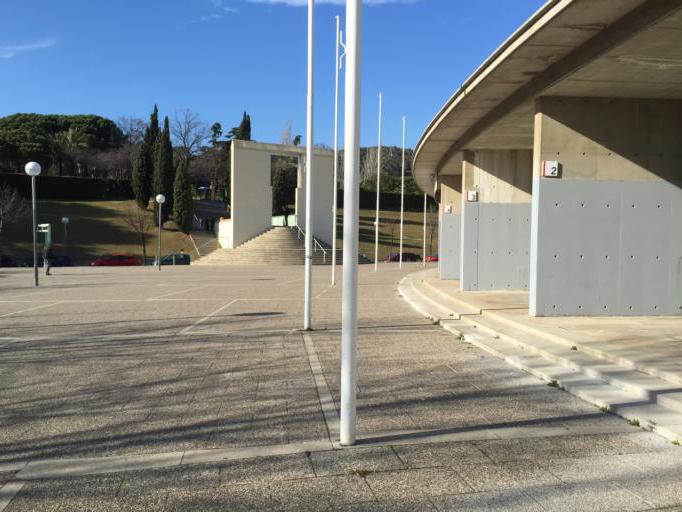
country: ES
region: Catalonia
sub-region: Provincia de Barcelona
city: Horta-Guinardo
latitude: 41.4378
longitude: 2.1482
